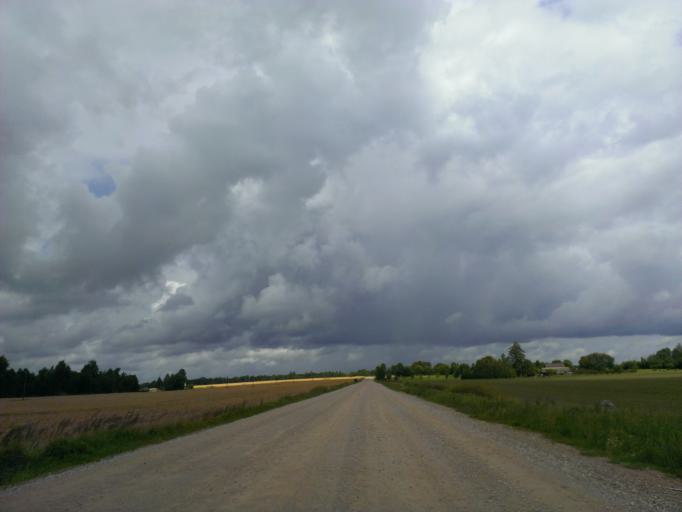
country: LV
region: Sigulda
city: Sigulda
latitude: 57.1868
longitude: 24.9388
